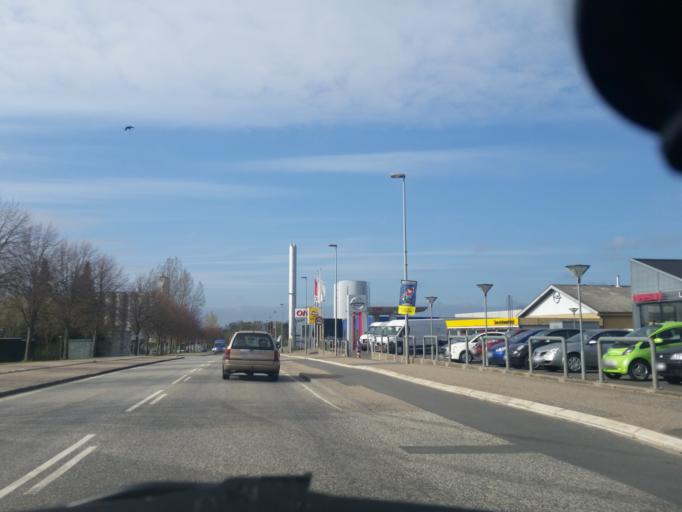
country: DK
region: Zealand
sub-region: Soro Kommune
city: Soro
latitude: 55.4418
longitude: 11.5660
